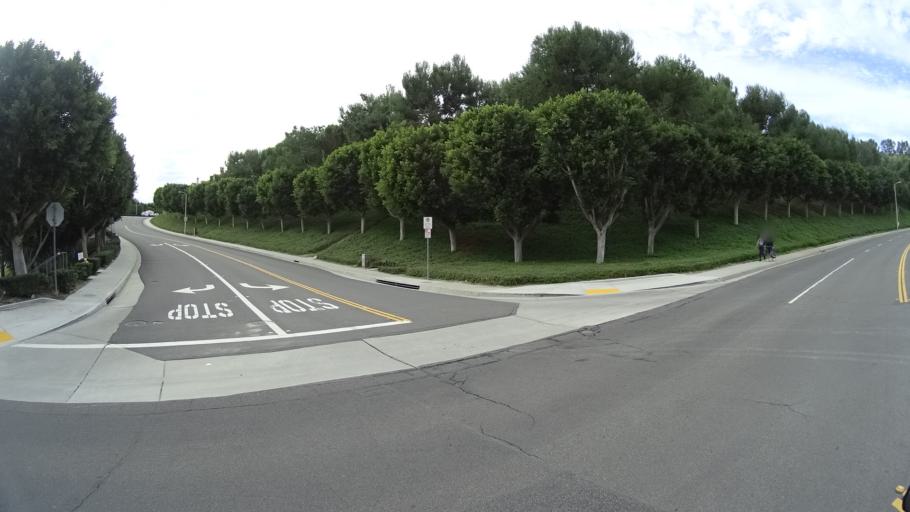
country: US
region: California
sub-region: Orange County
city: Aliso Viejo
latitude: 33.5585
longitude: -117.7281
